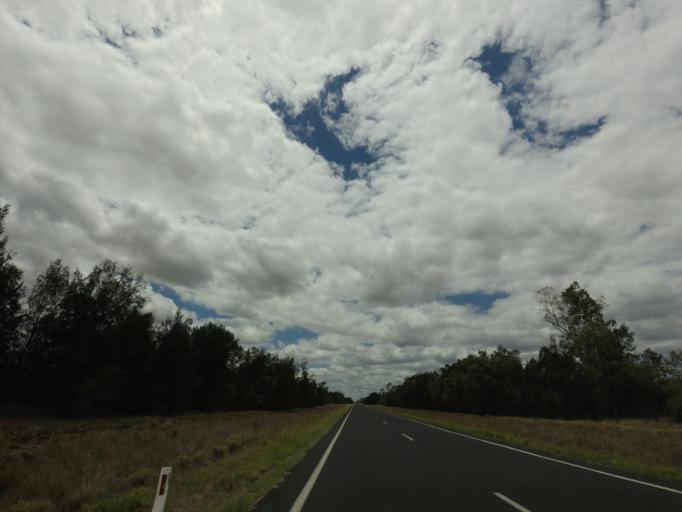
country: AU
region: Queensland
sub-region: Goondiwindi
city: Goondiwindi
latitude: -28.1691
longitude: 150.5893
